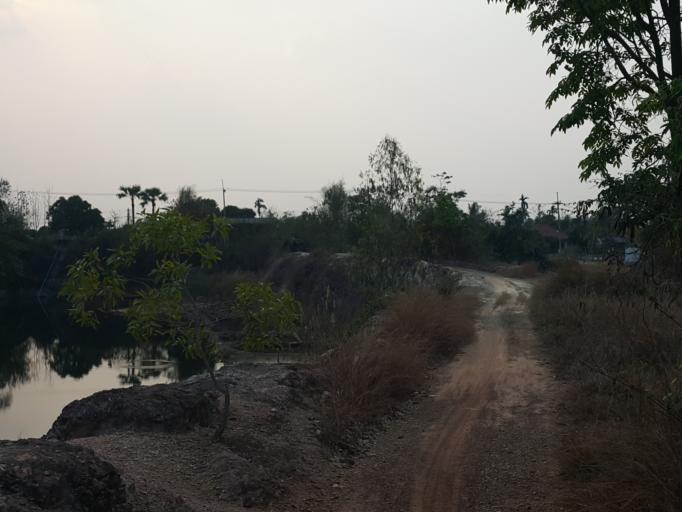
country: TH
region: Chiang Mai
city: San Kamphaeng
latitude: 18.7189
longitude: 99.1759
